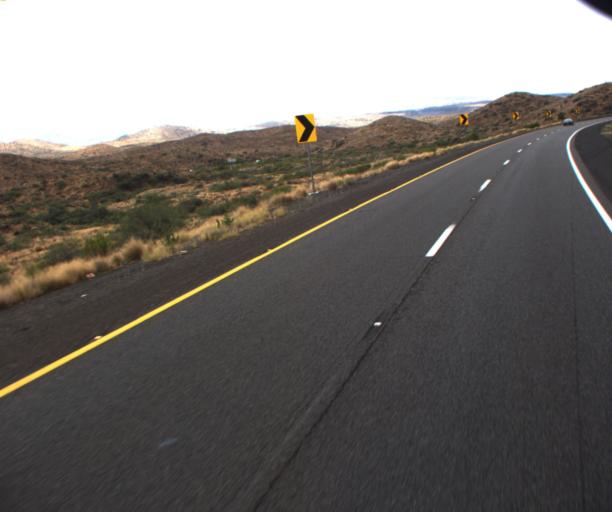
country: US
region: Arizona
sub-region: Yavapai County
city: Cordes Lakes
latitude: 34.2720
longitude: -112.1146
